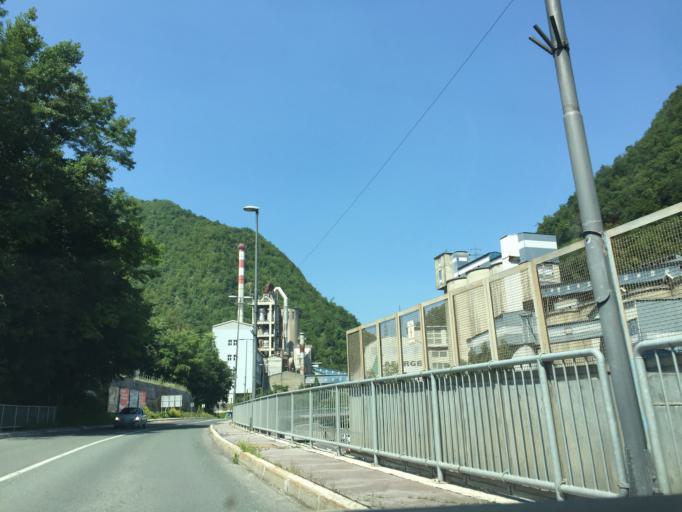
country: SI
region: Trbovlje
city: Trbovlje
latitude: 46.1259
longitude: 15.0359
